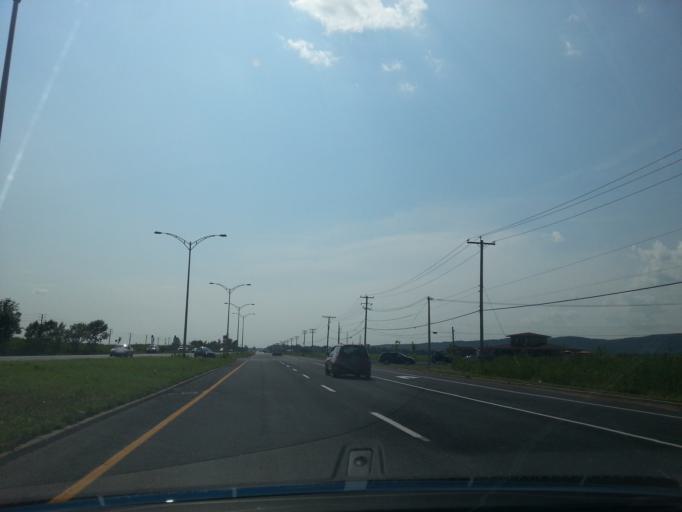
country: CA
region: Quebec
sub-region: Monteregie
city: Saint-Basile-le-Grand
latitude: 45.5402
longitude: -73.2510
